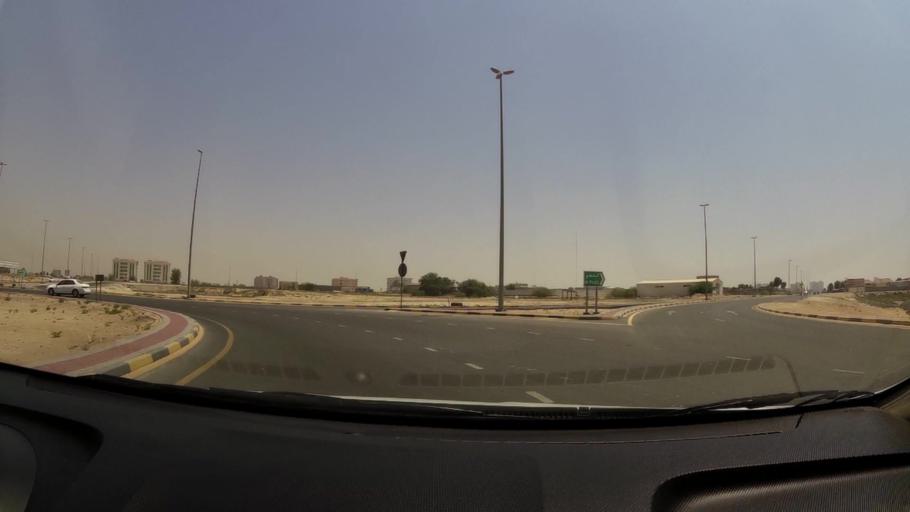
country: AE
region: Umm al Qaywayn
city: Umm al Qaywayn
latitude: 25.5019
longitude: 55.5693
